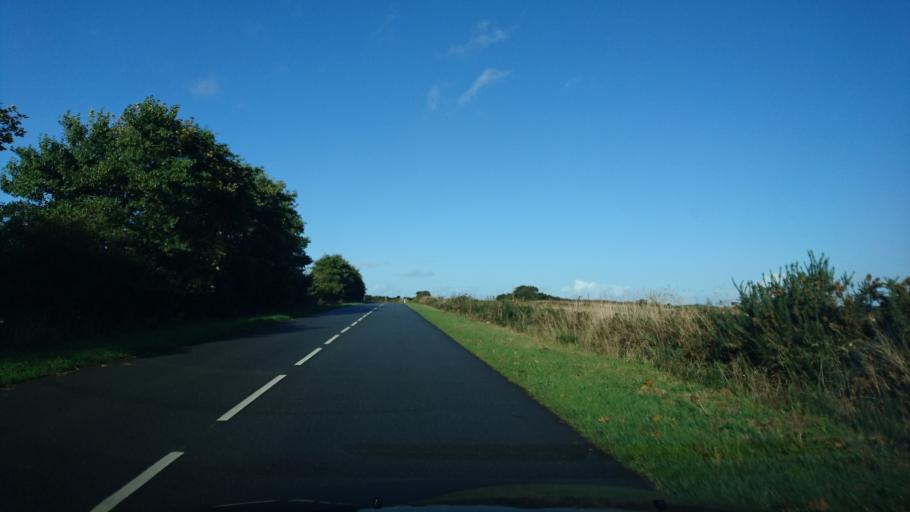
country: FR
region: Brittany
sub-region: Departement du Finistere
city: Plouarzel
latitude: 48.4393
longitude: -4.7345
